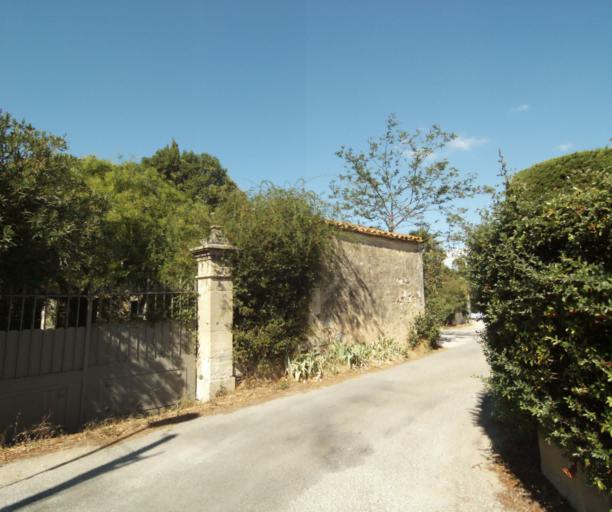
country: FR
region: Languedoc-Roussillon
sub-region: Departement du Gard
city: Bouillargues
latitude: 43.8013
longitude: 4.4307
